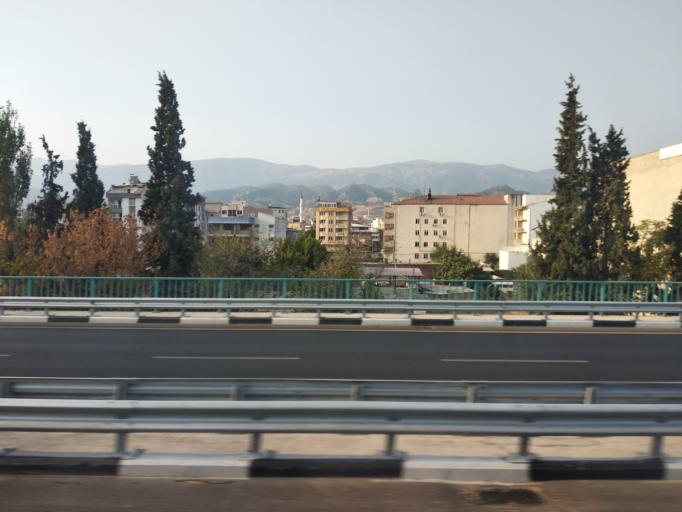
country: TR
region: Manisa
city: Salihli
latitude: 38.4904
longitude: 28.1411
